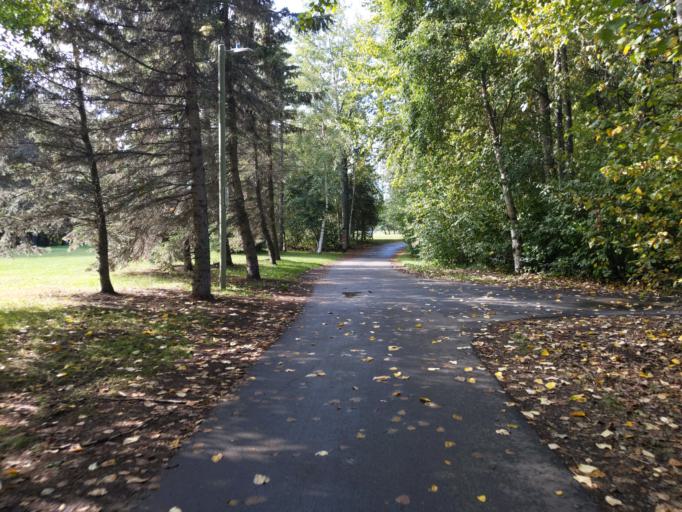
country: US
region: Alaska
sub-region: Anchorage Municipality
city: Anchorage
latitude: 61.2060
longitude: -149.9098
